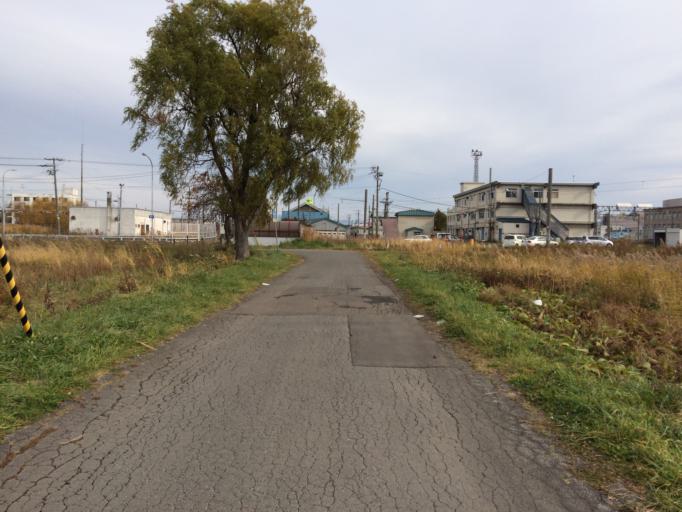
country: JP
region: Hokkaido
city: Iwamizawa
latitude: 43.2019
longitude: 141.7534
